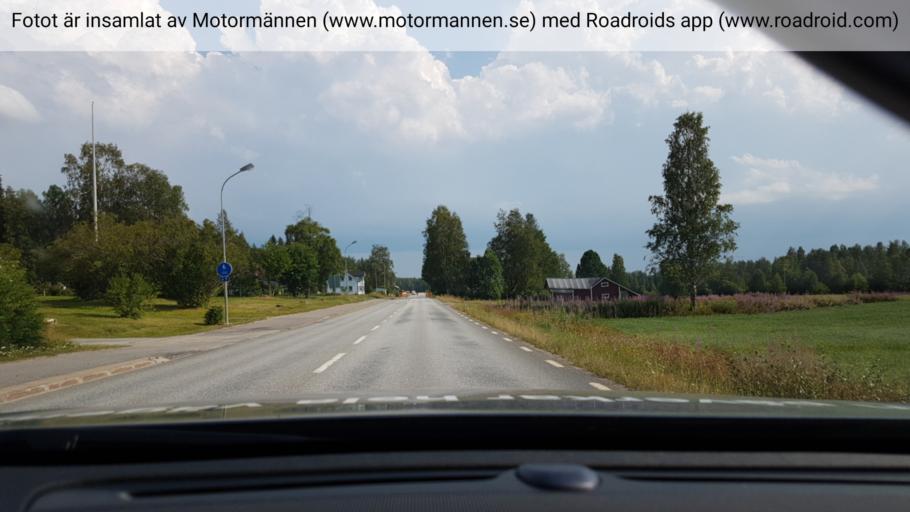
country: SE
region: Vaesterbotten
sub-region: Bjurholms Kommun
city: Bjurholm
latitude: 64.2458
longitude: 19.3216
